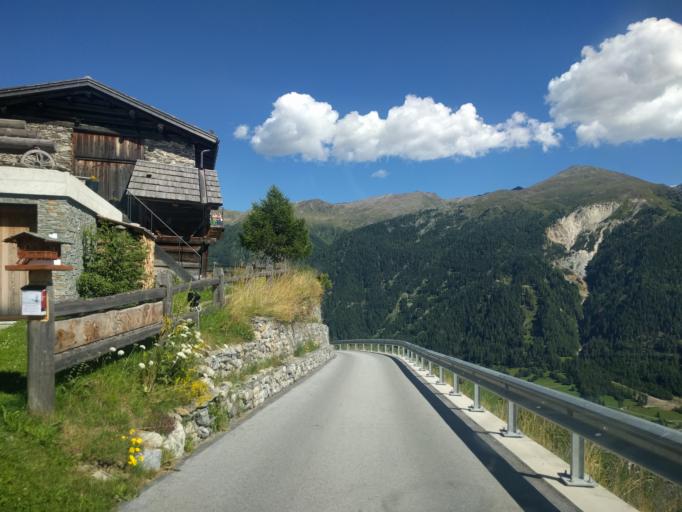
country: IT
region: Trentino-Alto Adige
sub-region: Bolzano
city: Tubre
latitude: 46.6087
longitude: 10.4095
